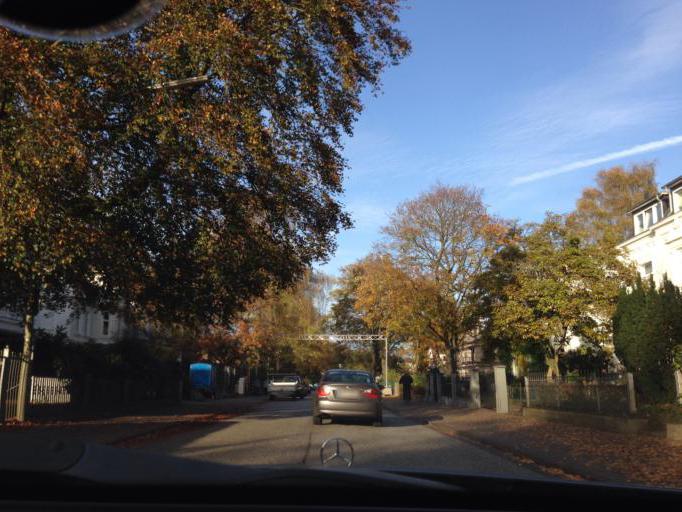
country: DE
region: Hamburg
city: Farmsen-Berne
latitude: 53.6068
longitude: 10.1559
